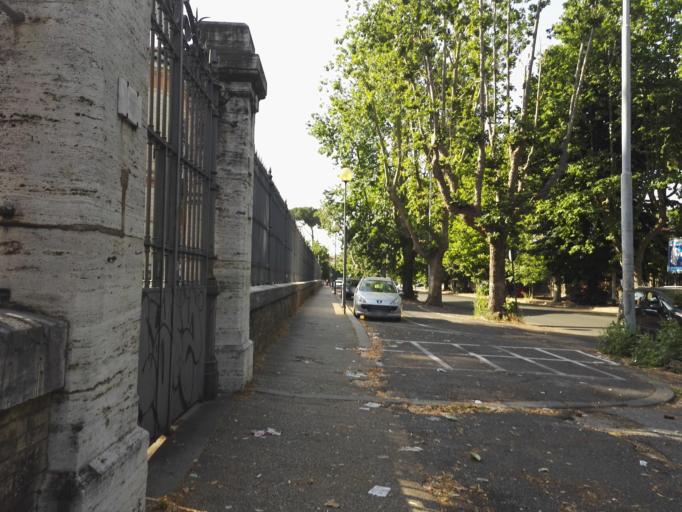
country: IT
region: Latium
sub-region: Citta metropolitana di Roma Capitale
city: Rome
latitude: 41.9052
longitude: 12.5104
